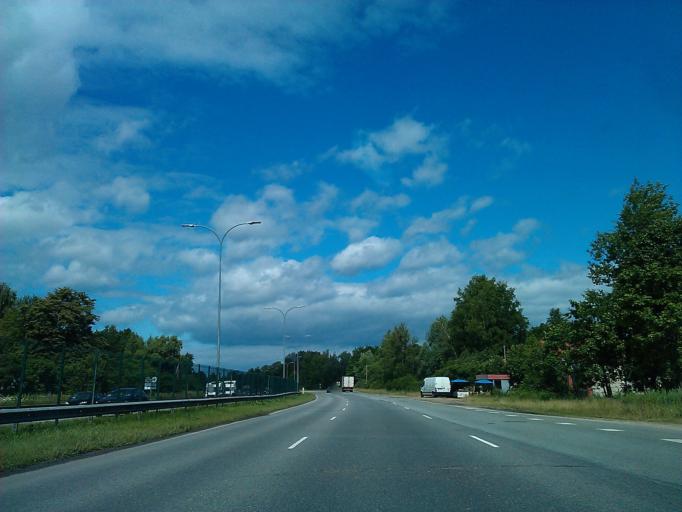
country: LV
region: Marupe
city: Marupe
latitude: 56.9465
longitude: 23.9928
